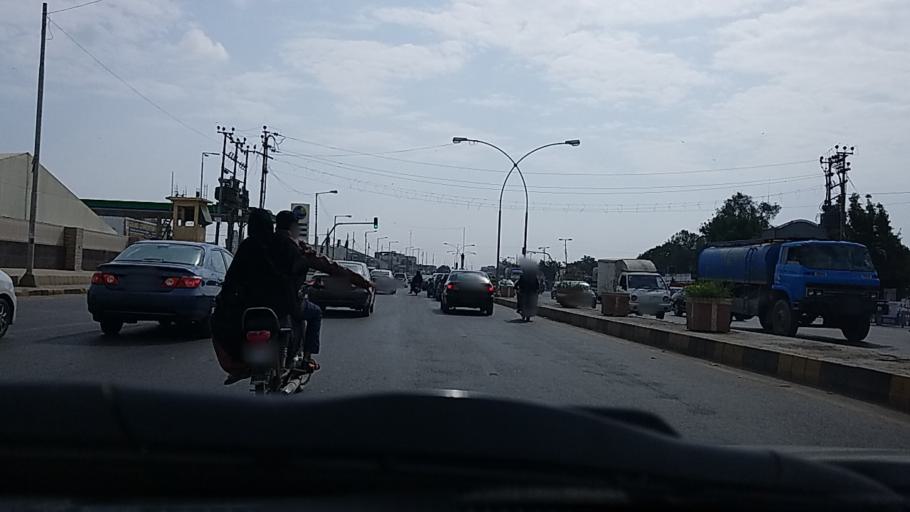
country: PK
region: Sindh
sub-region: Karachi District
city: Karachi
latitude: 24.8535
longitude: 67.0523
